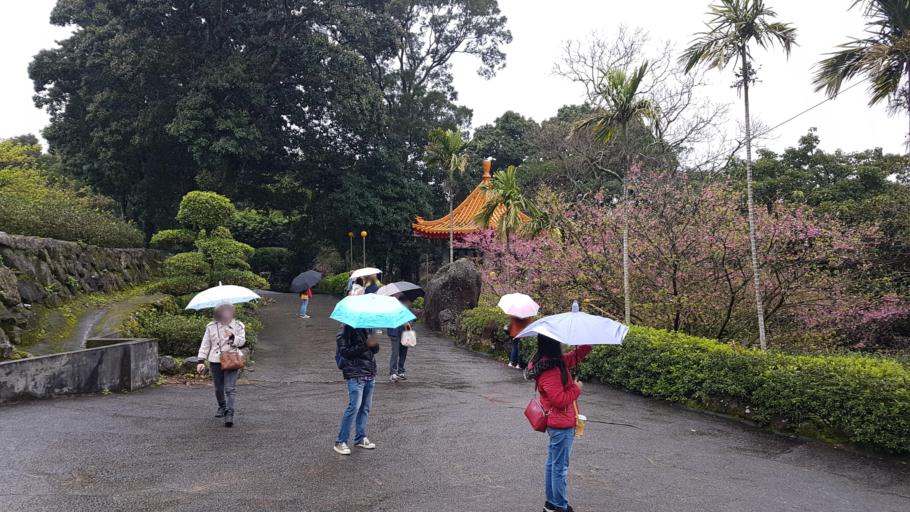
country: TW
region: Taipei
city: Taipei
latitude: 25.1846
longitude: 121.4883
